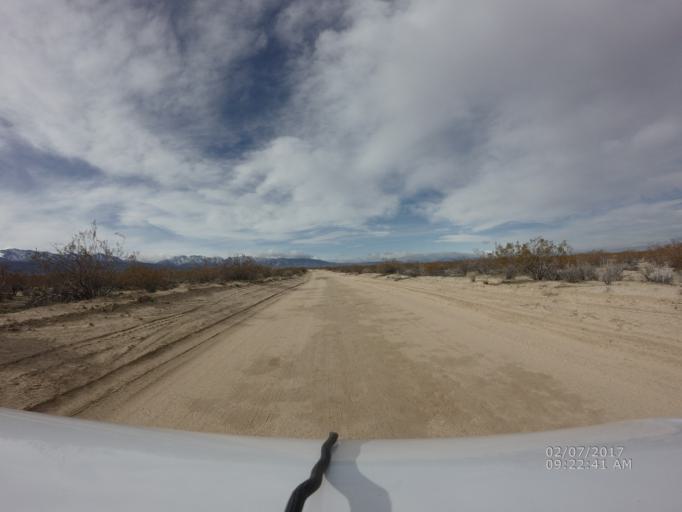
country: US
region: California
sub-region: San Bernardino County
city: Pinon Hills
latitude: 34.5210
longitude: -117.7344
